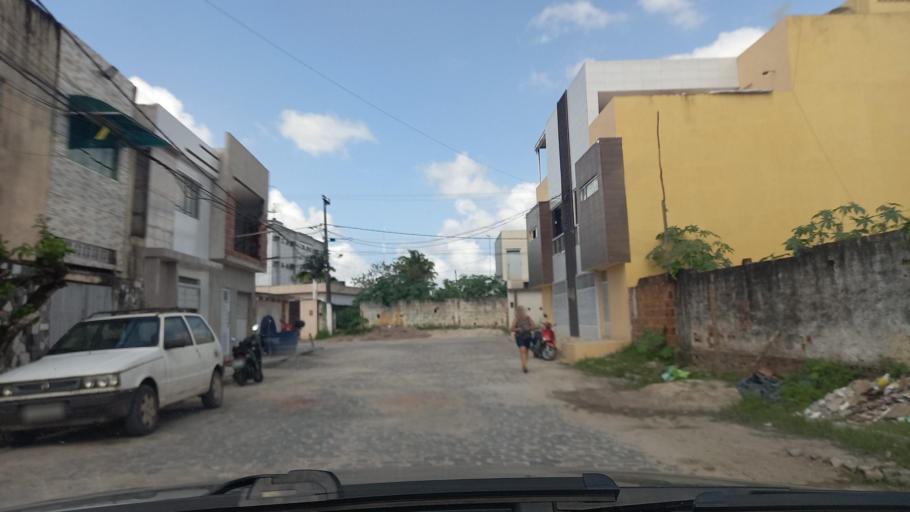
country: BR
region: Pernambuco
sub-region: Goiana
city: Goiana
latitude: -7.5636
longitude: -34.9965
